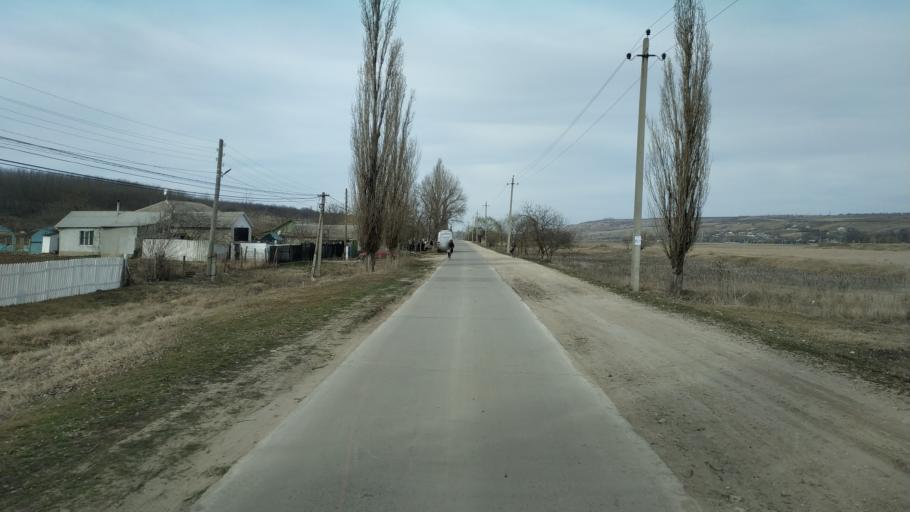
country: RO
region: Vaslui
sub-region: Comuna Dranceni
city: Dranceni
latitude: 46.8621
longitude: 28.2017
